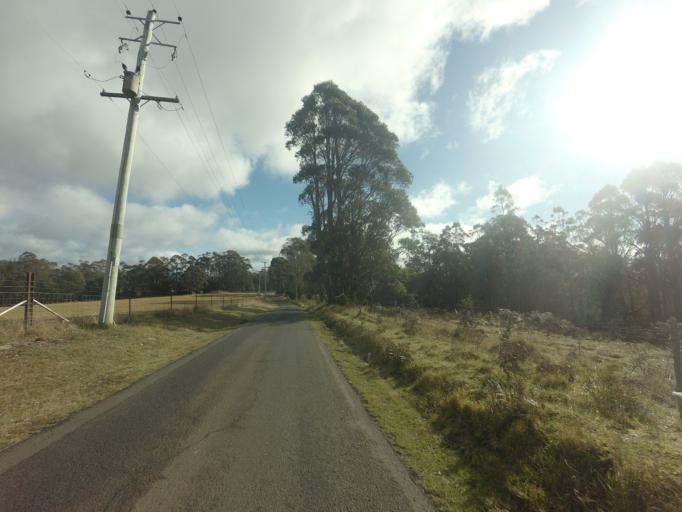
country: AU
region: Tasmania
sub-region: Derwent Valley
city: New Norfolk
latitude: -42.8441
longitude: 147.1444
